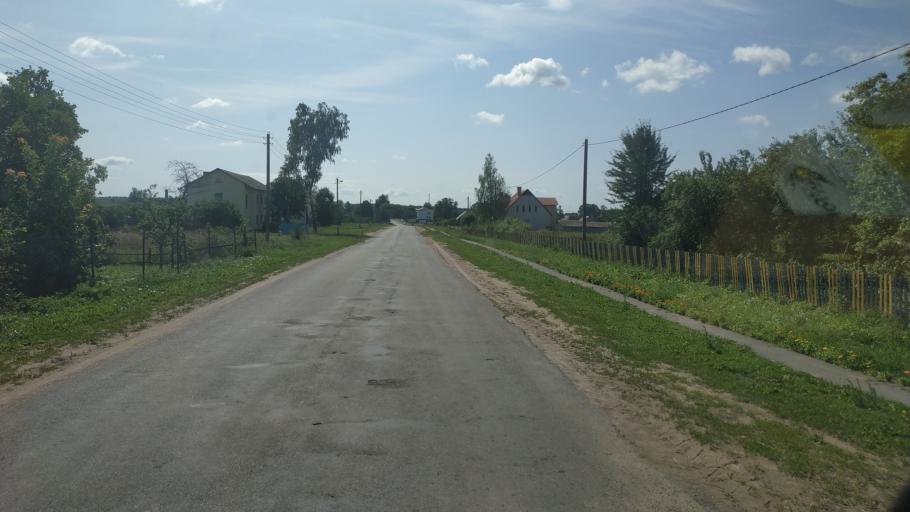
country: BY
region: Mogilev
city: Poselok Voskhod
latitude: 53.7078
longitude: 30.5012
